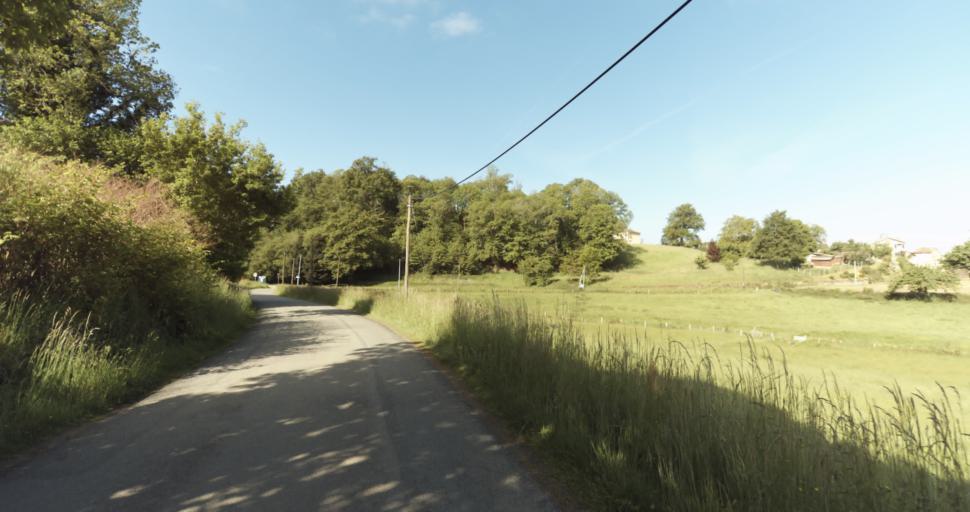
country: FR
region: Limousin
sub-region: Departement de la Haute-Vienne
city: Solignac
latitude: 45.7284
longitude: 1.2474
